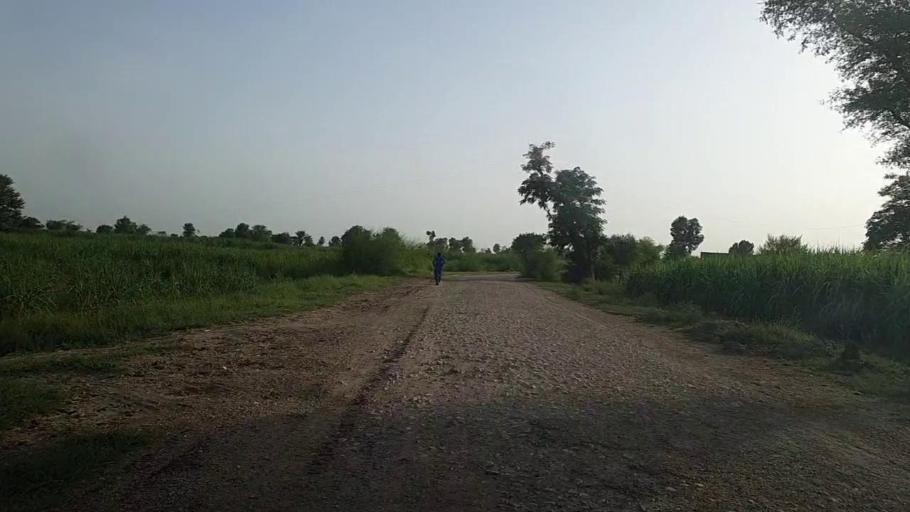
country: PK
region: Sindh
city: Naushahro Firoz
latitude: 26.8088
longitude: 68.1308
